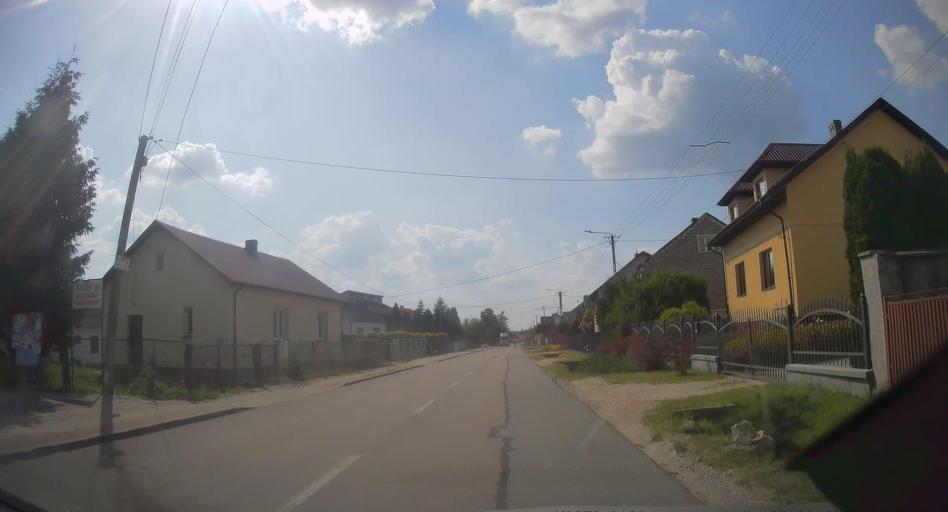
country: PL
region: Swietokrzyskie
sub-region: Powiat jedrzejowski
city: Malogoszcz
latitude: 50.8693
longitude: 20.2725
